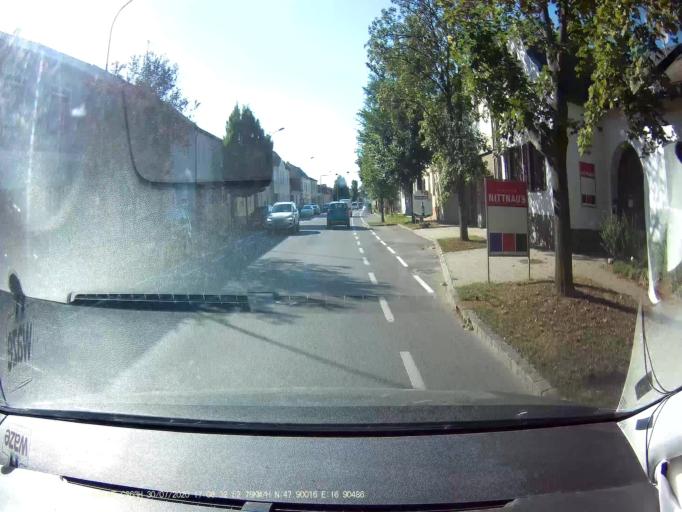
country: AT
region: Burgenland
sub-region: Politischer Bezirk Neusiedl am See
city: Gols
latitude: 47.9003
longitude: 16.9046
